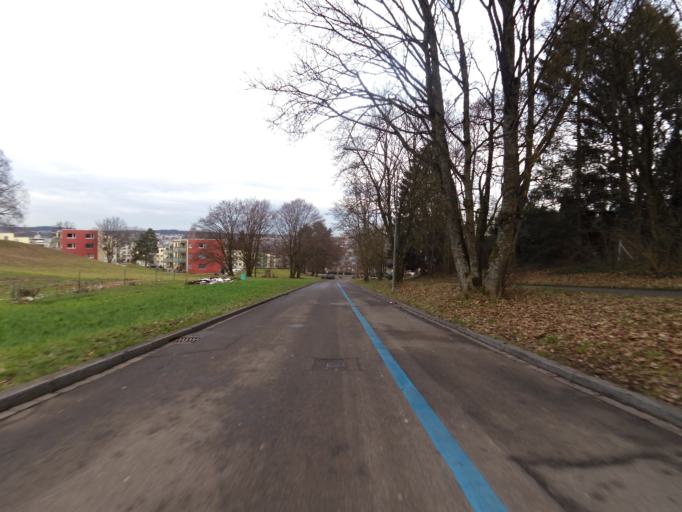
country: CH
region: Zurich
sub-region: Bezirk Zuerich
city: Zuerich (Kreis 9)
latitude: 47.3869
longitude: 8.4699
